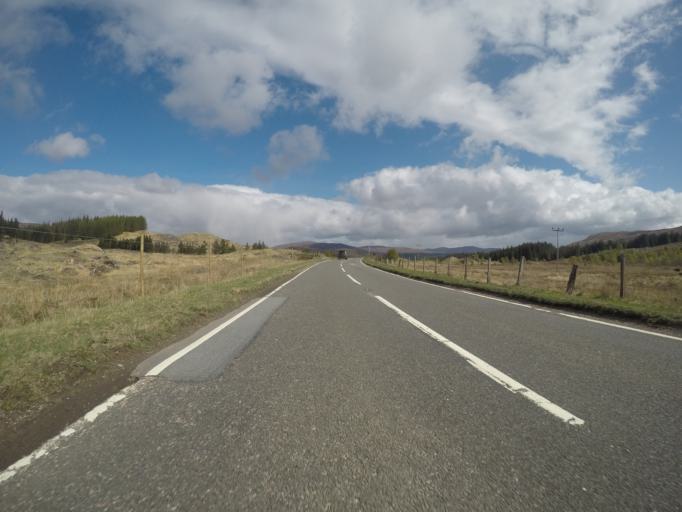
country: GB
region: Scotland
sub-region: Highland
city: Spean Bridge
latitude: 57.1369
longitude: -4.9547
